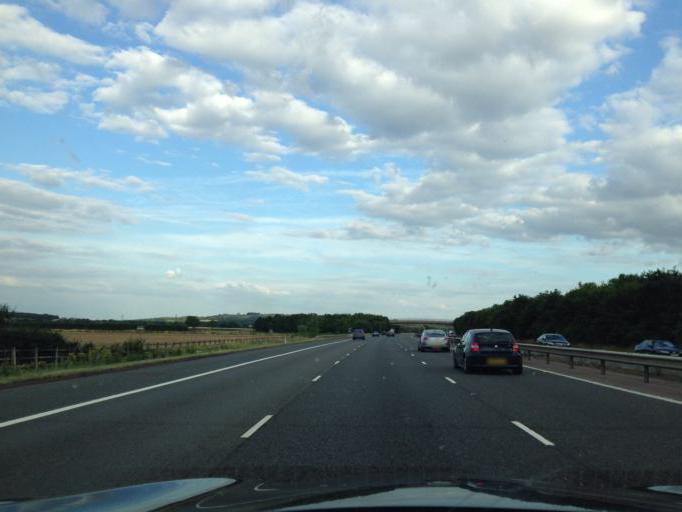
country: GB
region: England
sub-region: Oxfordshire
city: Bicester
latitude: 51.8432
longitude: -1.1482
